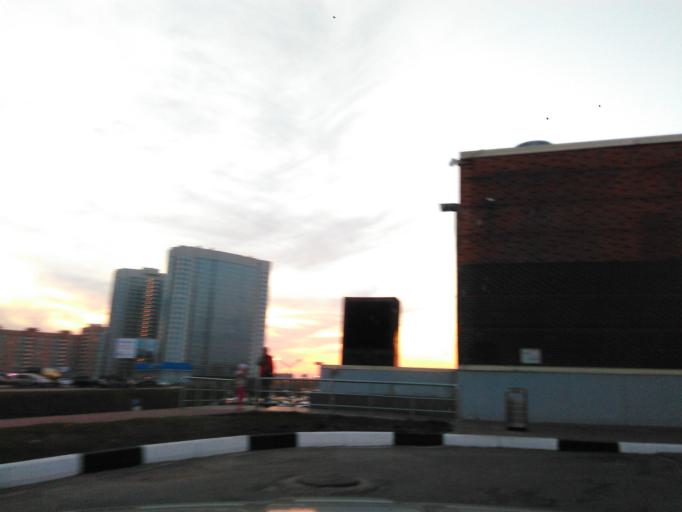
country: RU
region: Moscow
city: Khimki
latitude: 55.9085
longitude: 37.3971
